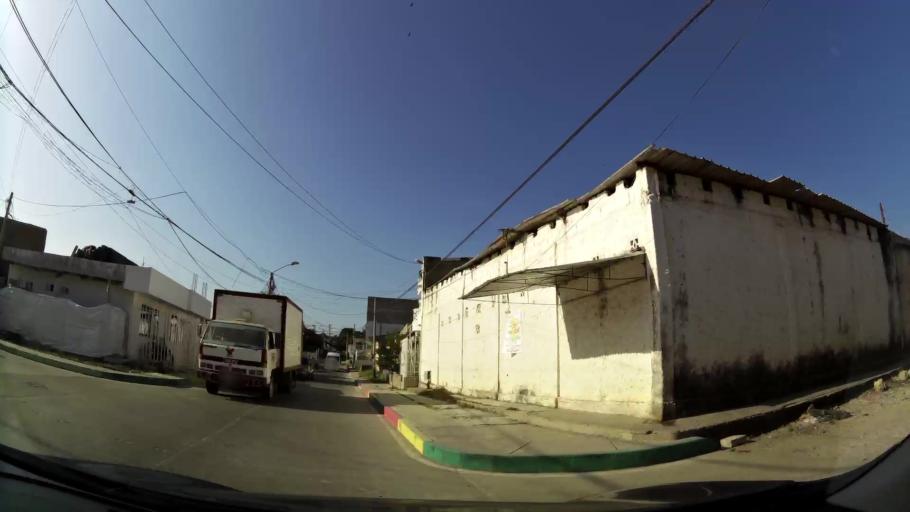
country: CO
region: Bolivar
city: Cartagena
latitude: 10.4012
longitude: -75.5005
